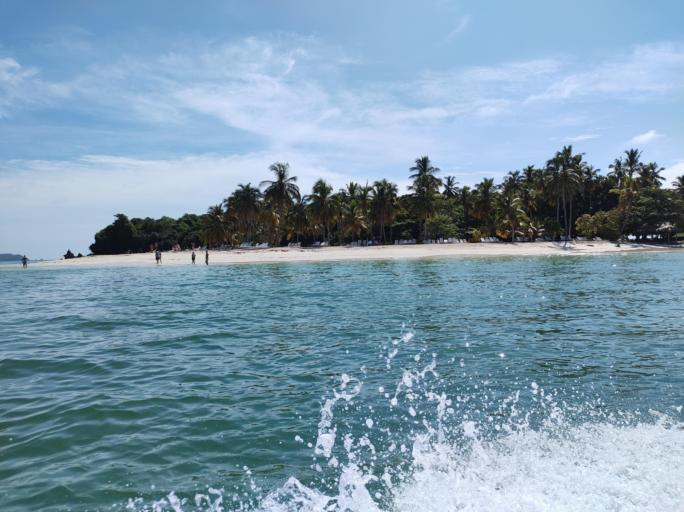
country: DO
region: Samana
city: Samana
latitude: 19.1683
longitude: -69.2804
